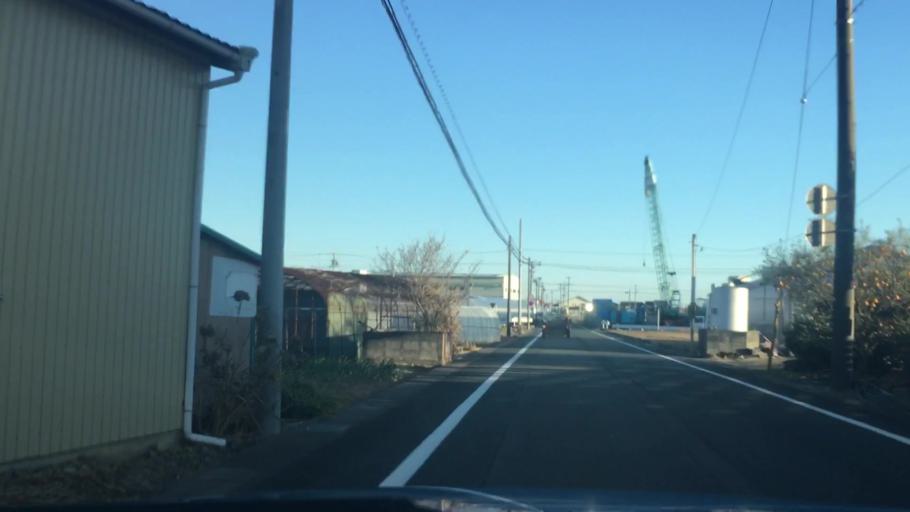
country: JP
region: Shizuoka
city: Hamamatsu
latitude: 34.7408
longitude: 137.6702
